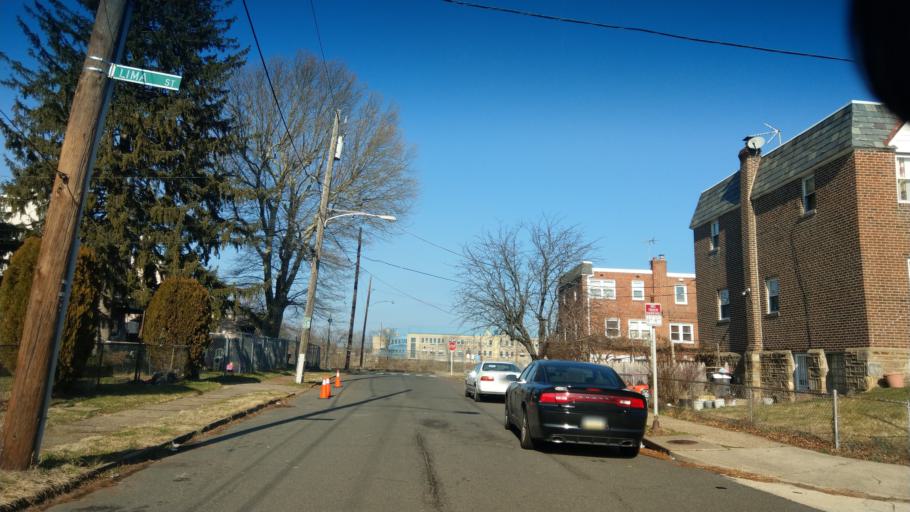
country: US
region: Pennsylvania
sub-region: Montgomery County
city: Rockledge
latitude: 40.0328
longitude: -75.1194
